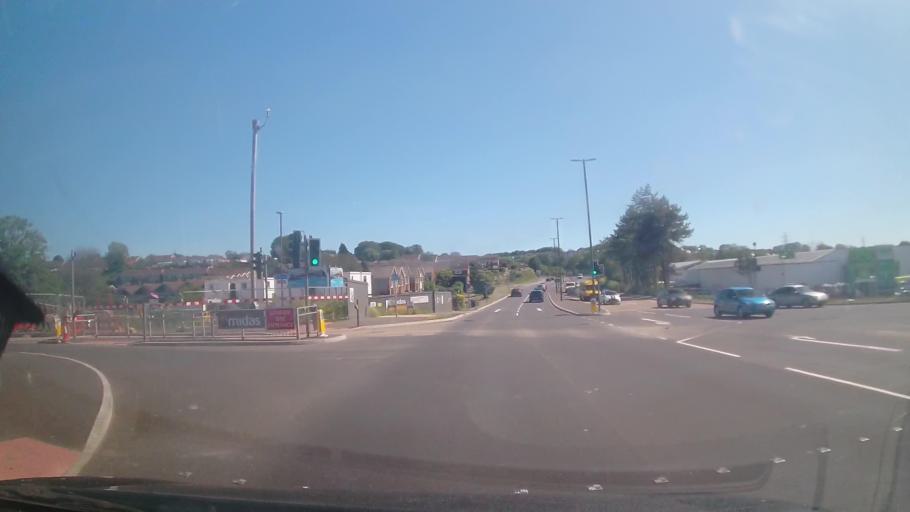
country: GB
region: England
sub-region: Borough of Torbay
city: Paignton
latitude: 50.4248
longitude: -3.5872
